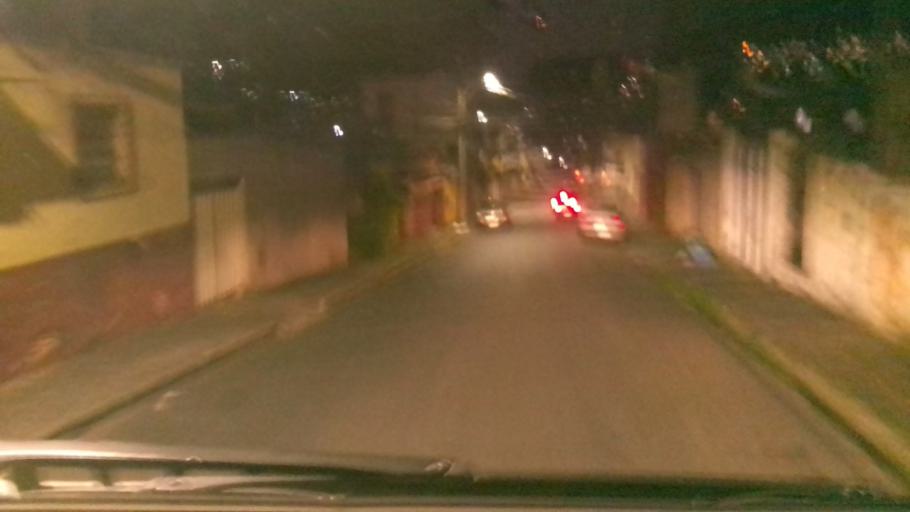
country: BR
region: Minas Gerais
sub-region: Belo Horizonte
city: Belo Horizonte
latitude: -19.9112
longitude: -43.9025
